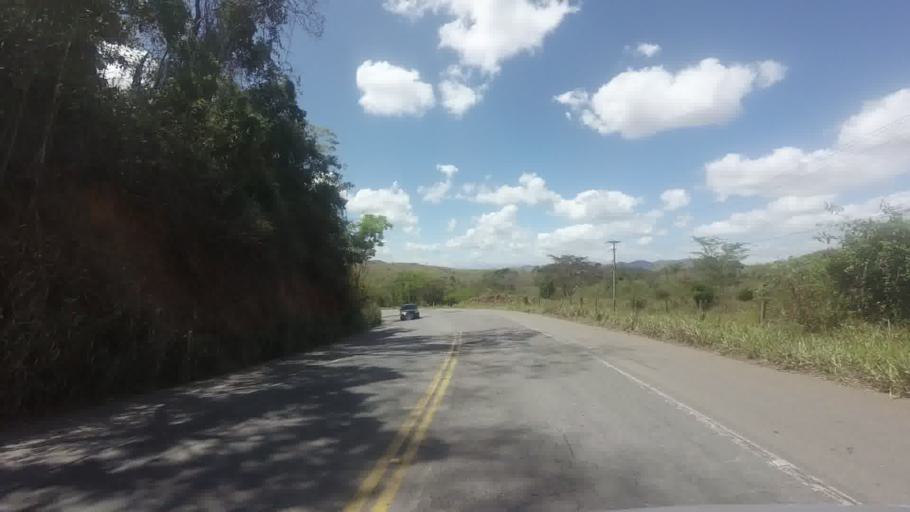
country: BR
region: Rio de Janeiro
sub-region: Santo Antonio De Padua
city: Santo Antonio de Padua
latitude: -21.6588
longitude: -42.3113
